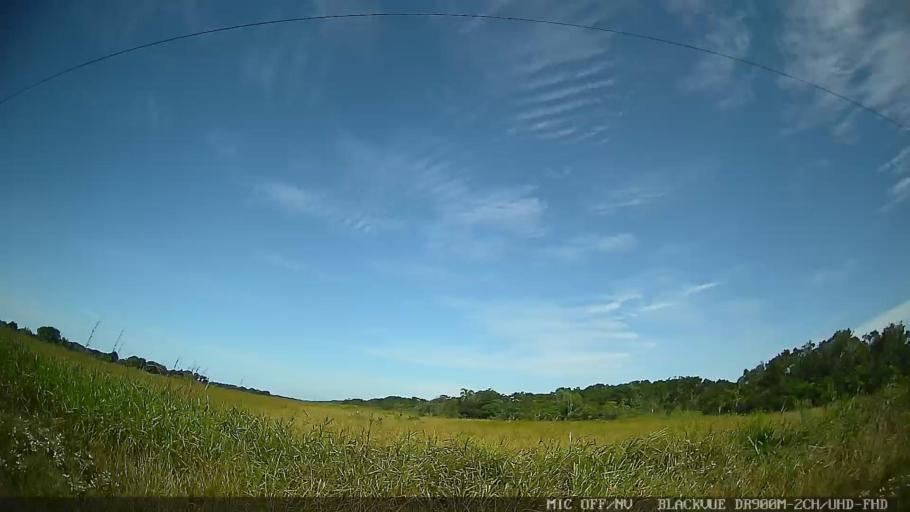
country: BR
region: Sao Paulo
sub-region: Iguape
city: Iguape
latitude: -24.7778
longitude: -47.6085
